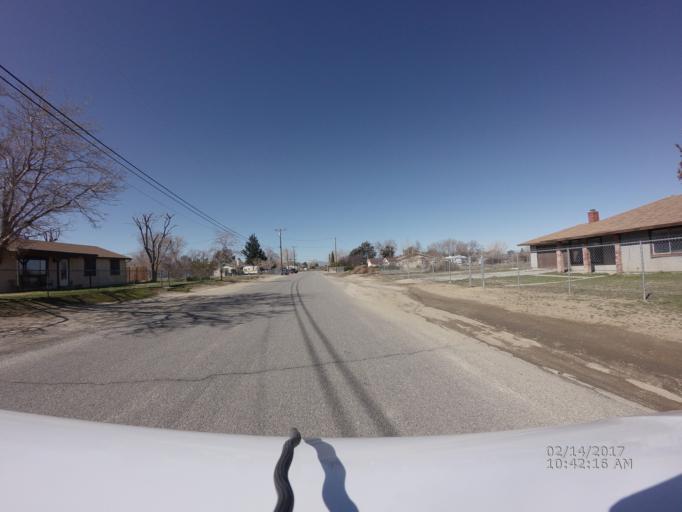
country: US
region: California
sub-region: Los Angeles County
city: Littlerock
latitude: 34.5634
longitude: -117.9504
